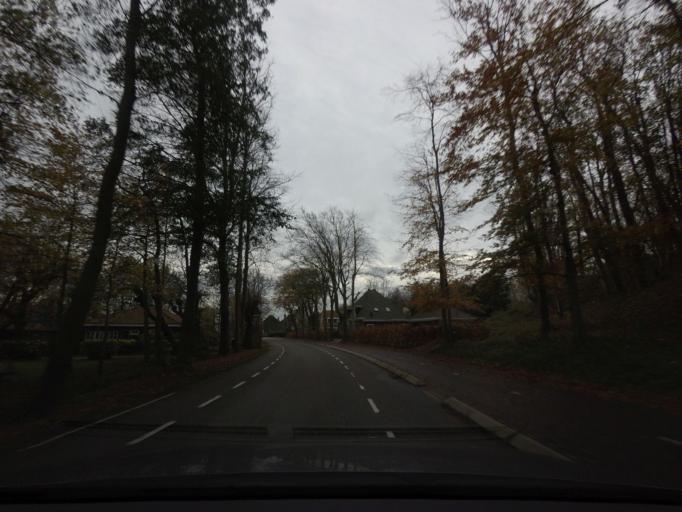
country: NL
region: North Holland
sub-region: Gemeente Bergen
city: Egmond aan Zee
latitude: 52.6376
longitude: 4.6571
